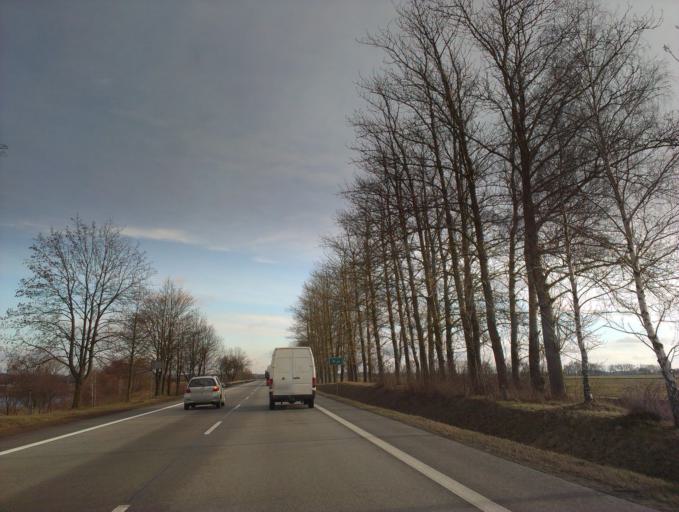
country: PL
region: Kujawsko-Pomorskie
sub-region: Powiat lipnowski
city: Kikol
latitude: 52.9292
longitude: 19.0756
